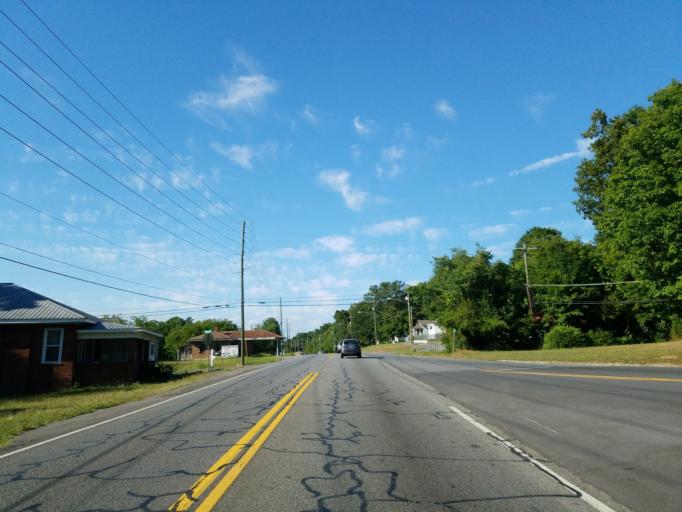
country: US
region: Georgia
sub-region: Gordon County
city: Calhoun
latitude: 34.5198
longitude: -84.9426
